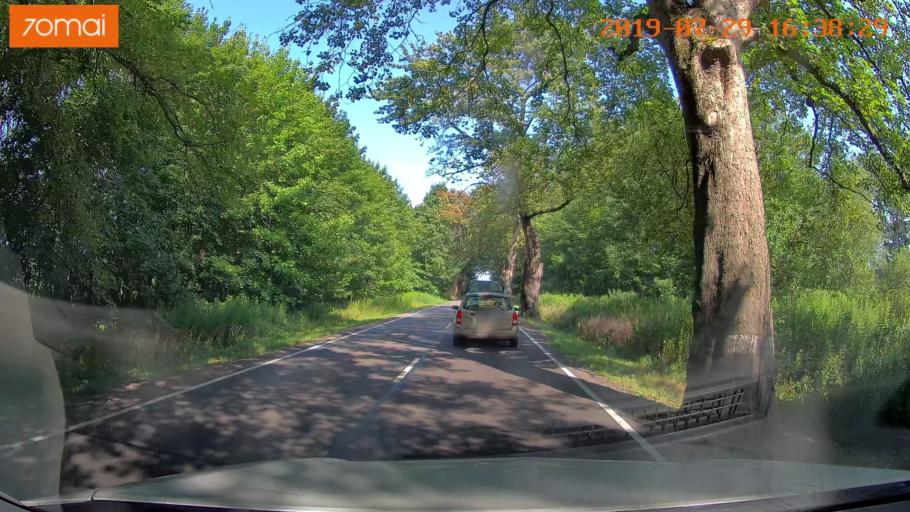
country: RU
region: Kaliningrad
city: Primorsk
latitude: 54.7402
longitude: 20.0617
